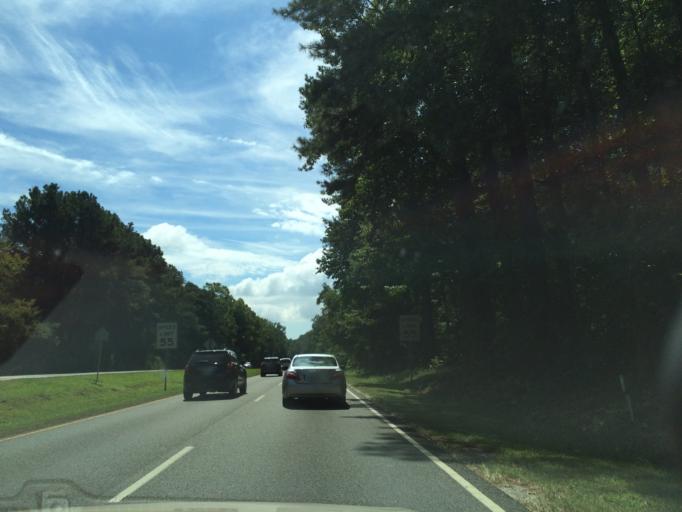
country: US
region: Virginia
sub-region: York County
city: Yorktown
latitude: 37.2228
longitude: -76.5154
